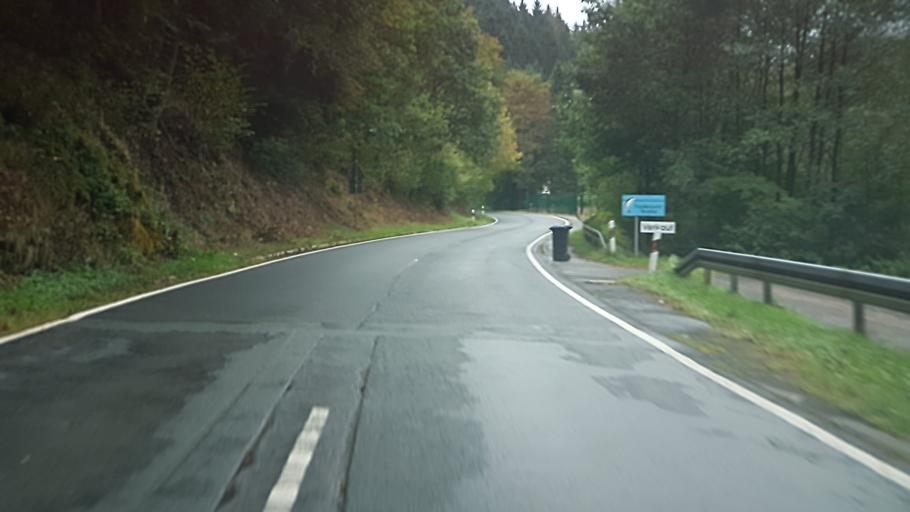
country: DE
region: North Rhine-Westphalia
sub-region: Regierungsbezirk Arnsberg
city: Herscheid
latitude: 51.1975
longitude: 7.6933
